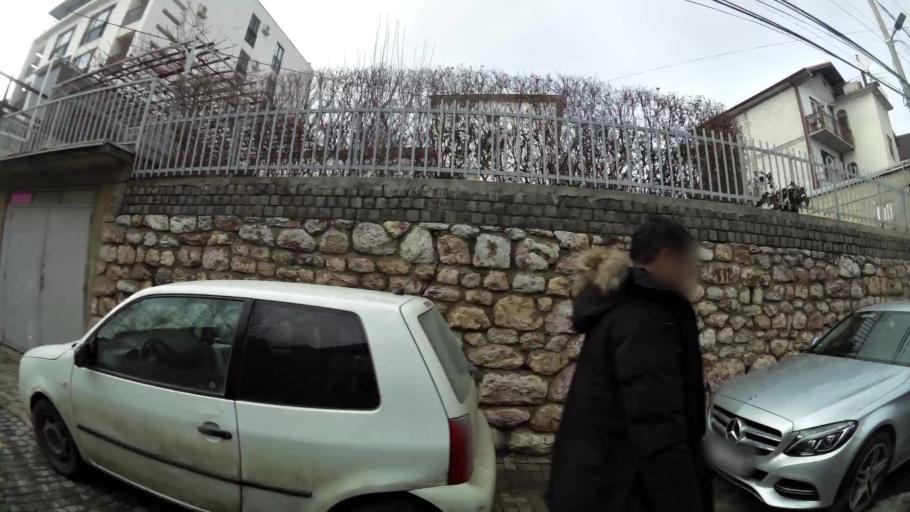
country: XK
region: Pristina
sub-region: Komuna e Prishtines
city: Pristina
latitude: 42.6642
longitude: 21.1518
